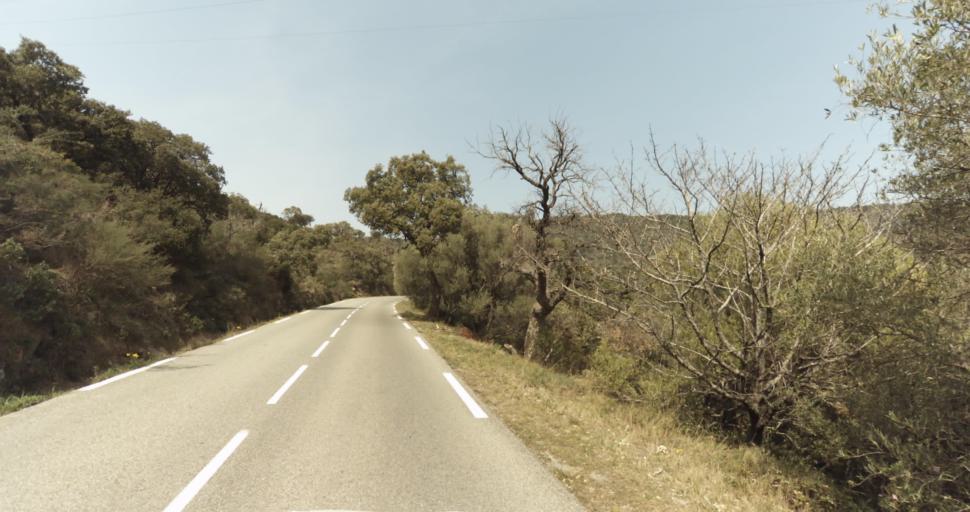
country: FR
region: Provence-Alpes-Cote d'Azur
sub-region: Departement du Var
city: Bormes-les-Mimosas
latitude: 43.1585
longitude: 6.3440
